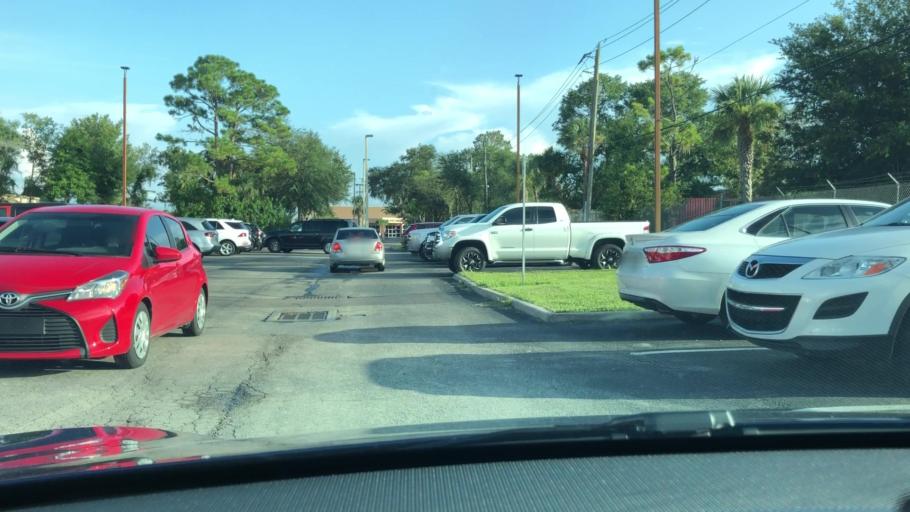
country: US
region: Florida
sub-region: Seminole County
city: Sanford
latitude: 28.7806
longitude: -81.2854
